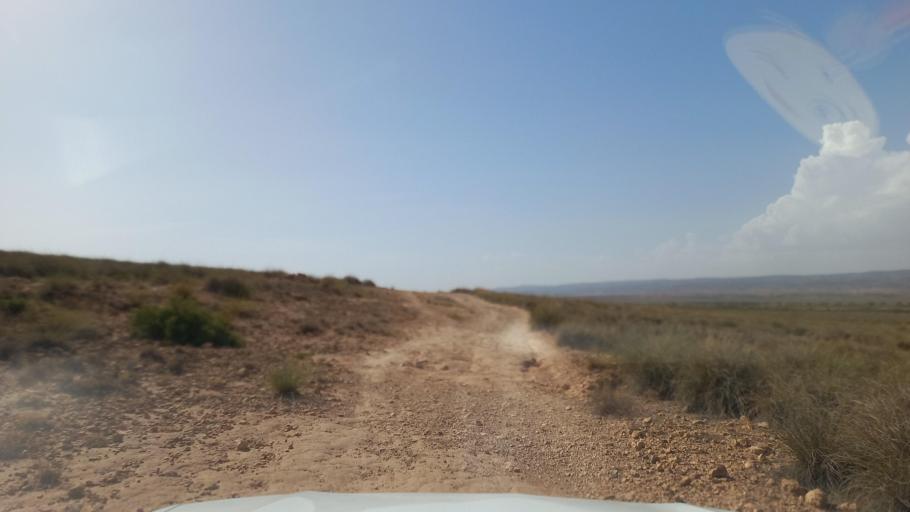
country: TN
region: Al Qasrayn
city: Kasserine
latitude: 35.2152
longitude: 8.9877
